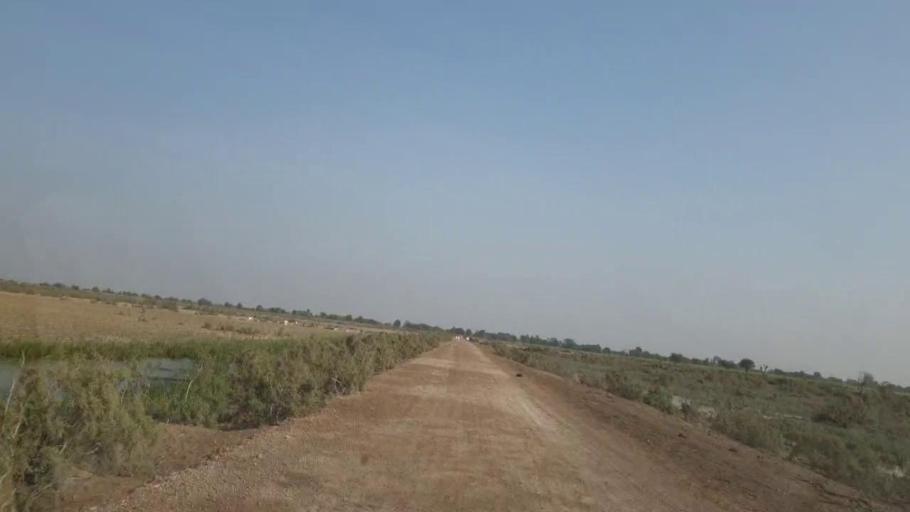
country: PK
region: Sindh
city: Pithoro
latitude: 25.6961
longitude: 69.2292
